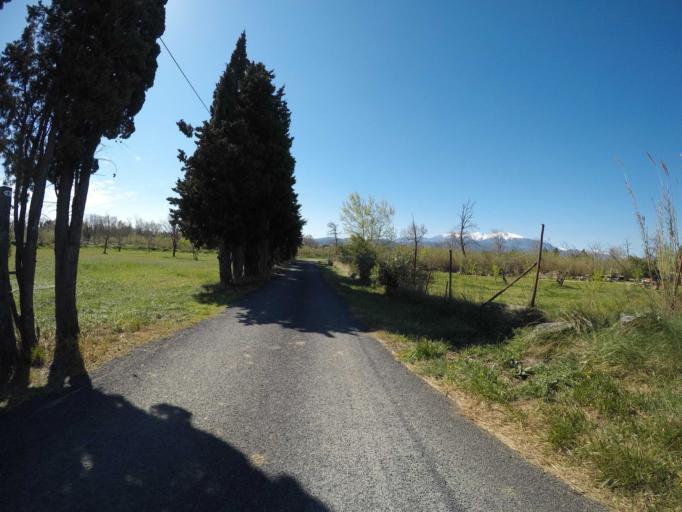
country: FR
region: Languedoc-Roussillon
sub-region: Departement des Pyrenees-Orientales
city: Millas
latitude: 42.6995
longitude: 2.6657
